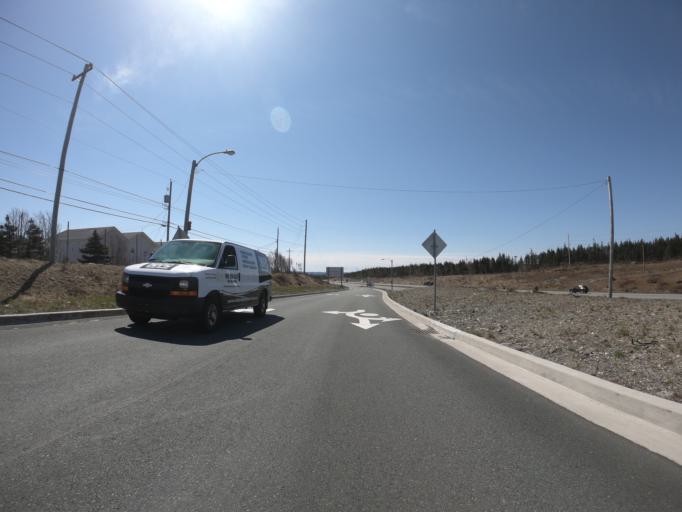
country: CA
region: Newfoundland and Labrador
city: Mount Pearl
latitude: 47.5077
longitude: -52.8227
